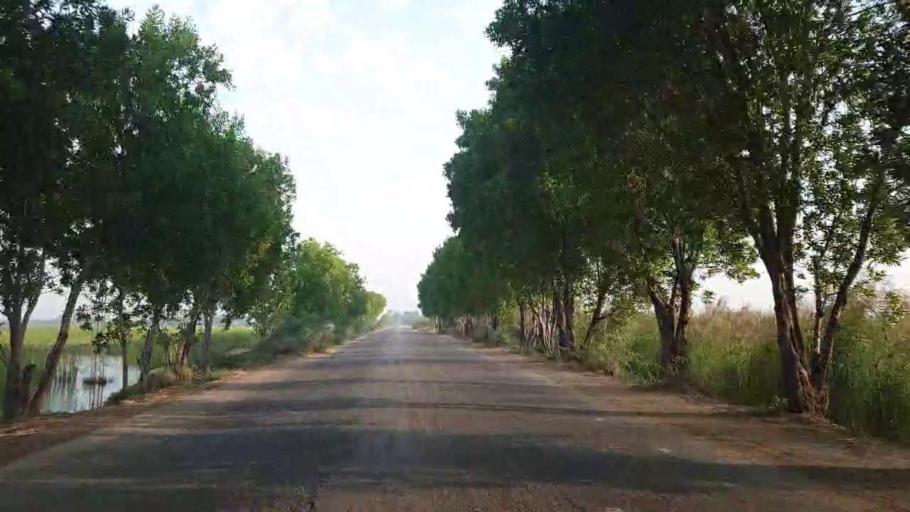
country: PK
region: Sindh
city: Tando Bago
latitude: 24.7362
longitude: 68.9457
